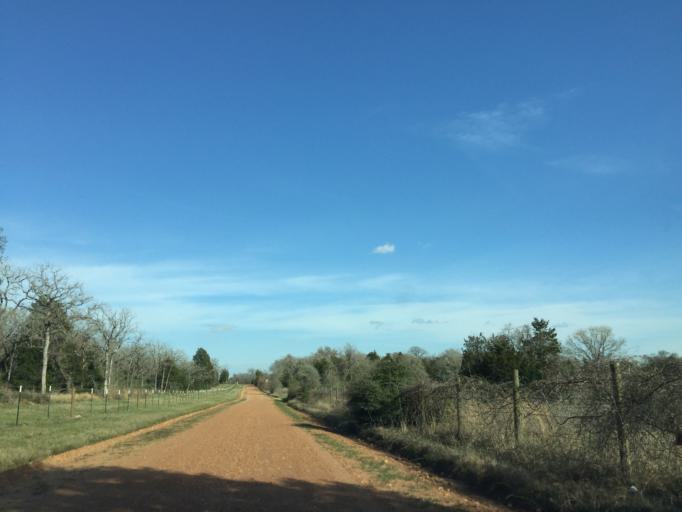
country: US
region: Texas
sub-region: Lee County
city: Lexington
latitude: 30.4459
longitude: -97.1751
